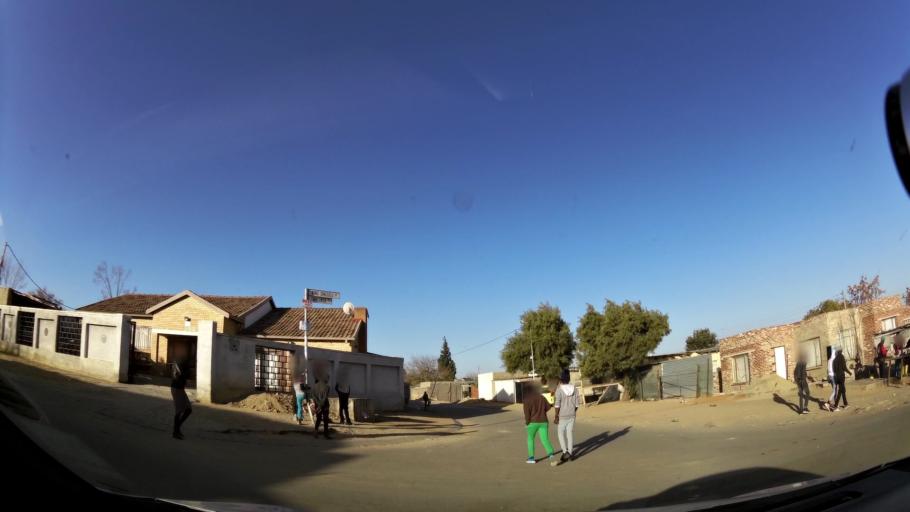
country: ZA
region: Gauteng
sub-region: City of Johannesburg Metropolitan Municipality
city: Diepsloot
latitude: -25.9193
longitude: 28.0209
